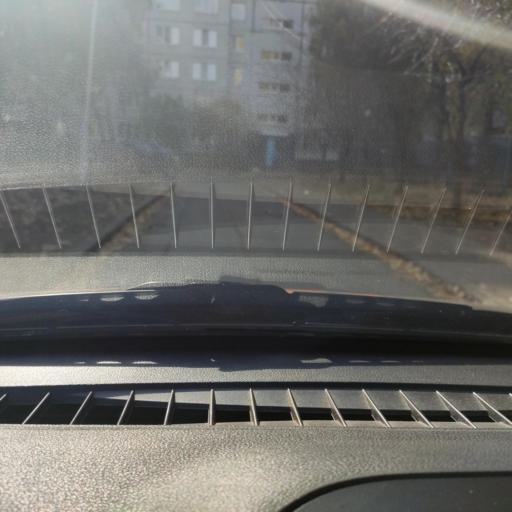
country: RU
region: Samara
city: Tol'yatti
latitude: 53.5354
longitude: 49.2872
